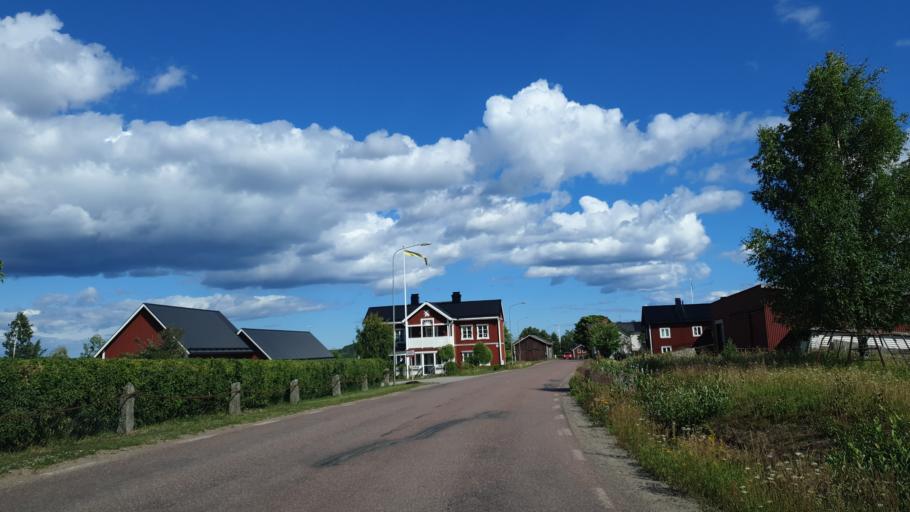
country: SE
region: Gaevleborg
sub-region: Nordanstigs Kommun
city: Bergsjoe
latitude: 62.0527
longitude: 17.1973
